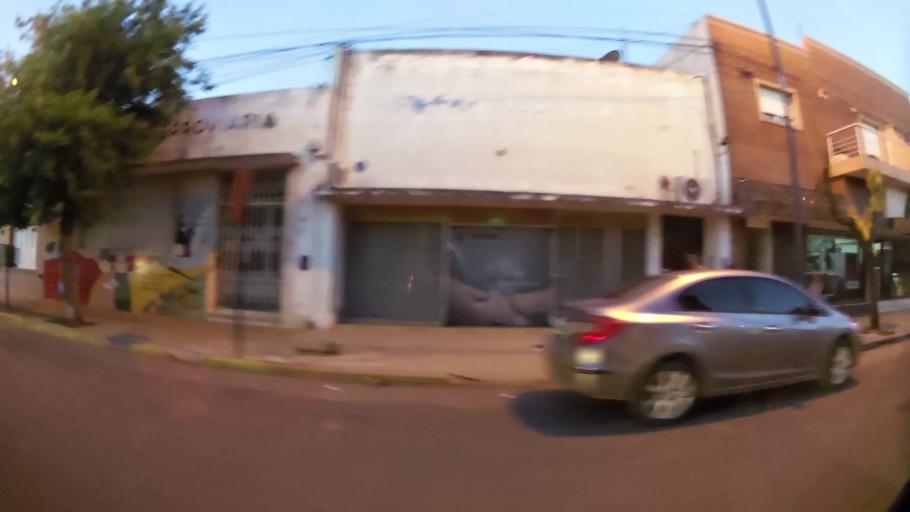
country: AR
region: Cordoba
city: Villa Maria
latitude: -32.4084
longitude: -63.2477
